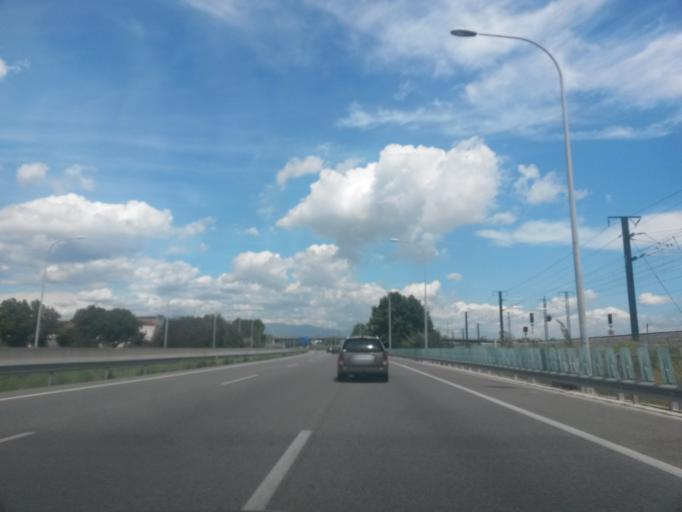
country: ES
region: Catalonia
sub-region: Provincia de Barcelona
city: Mollet del Valles
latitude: 41.5355
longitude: 2.2237
